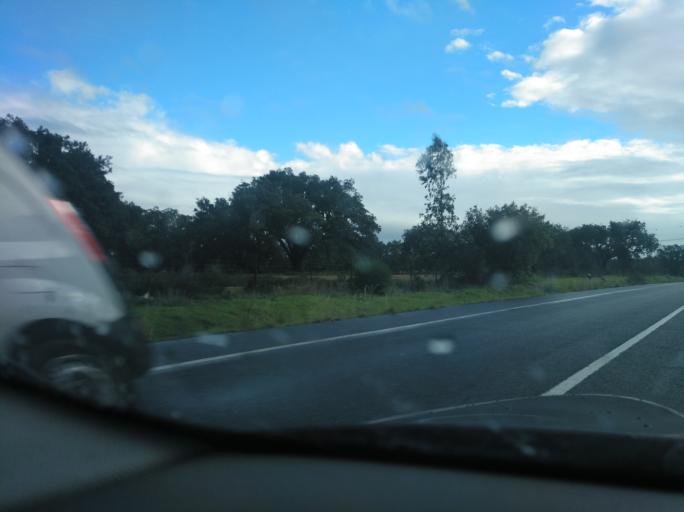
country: PT
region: Setubal
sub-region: Grandola
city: Grandola
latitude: 38.0243
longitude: -8.3994
